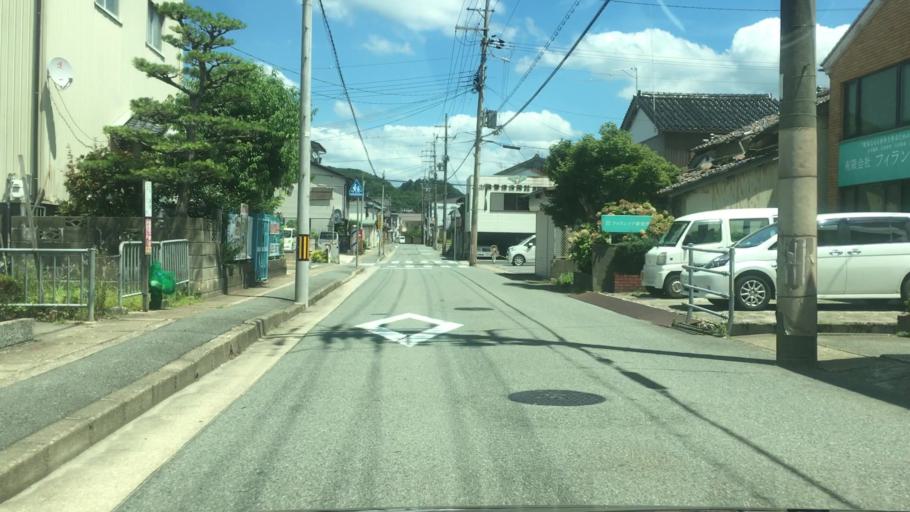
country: JP
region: Hyogo
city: Toyooka
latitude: 35.5490
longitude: 134.8213
